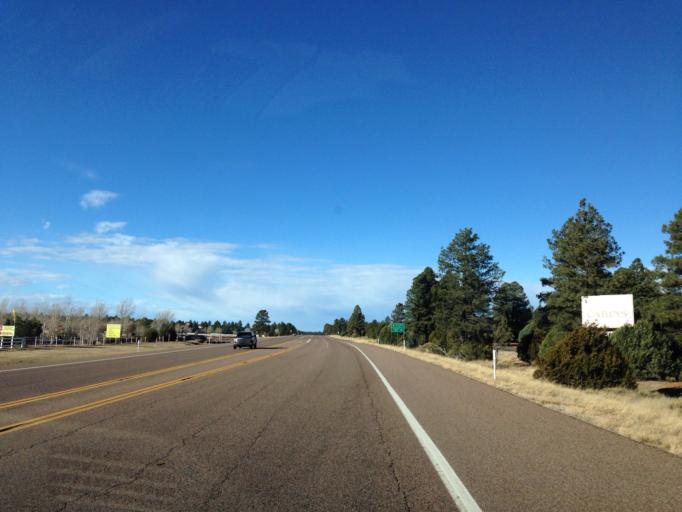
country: US
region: Arizona
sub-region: Navajo County
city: Heber-Overgaard
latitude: 34.3932
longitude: -110.5255
